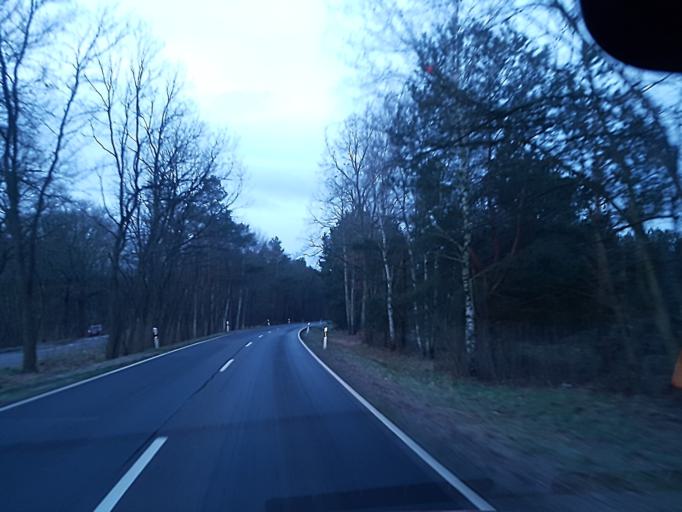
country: DE
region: Brandenburg
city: Finsterwalde
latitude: 51.5838
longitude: 13.7016
